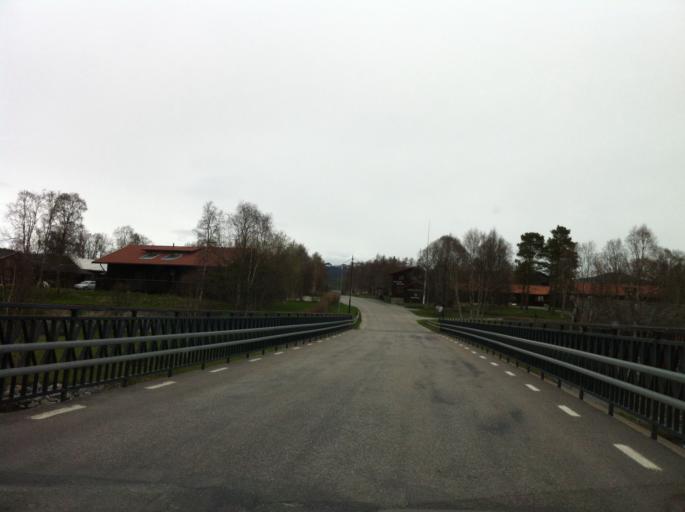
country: NO
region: Hedmark
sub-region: Engerdal
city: Engerdal
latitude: 62.5266
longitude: 12.5941
